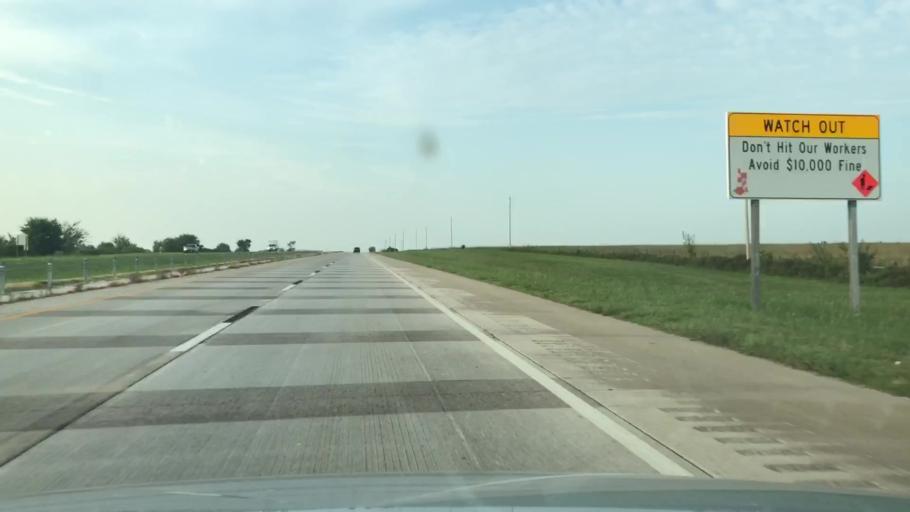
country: US
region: Oklahoma
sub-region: Osage County
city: Skiatook
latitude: 36.4221
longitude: -95.9207
